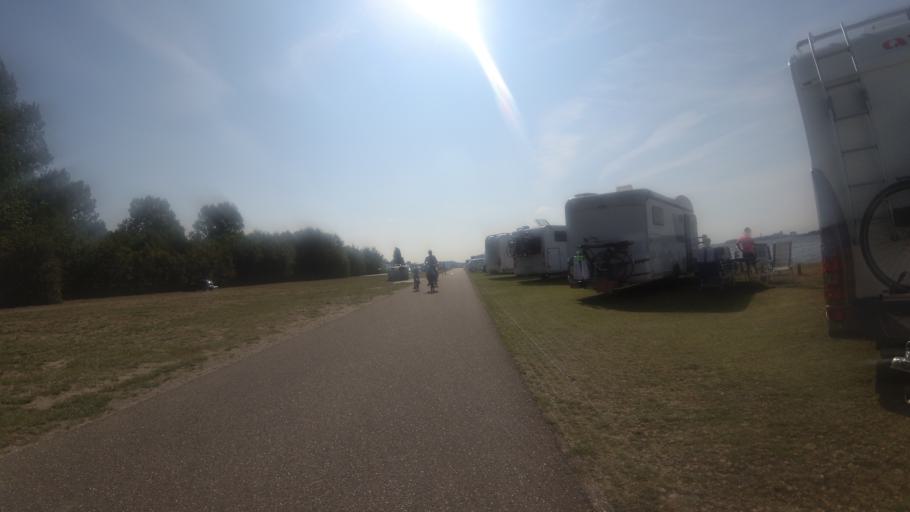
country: NL
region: Zeeland
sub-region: Gemeente Veere
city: Veere
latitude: 51.5700
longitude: 3.6539
